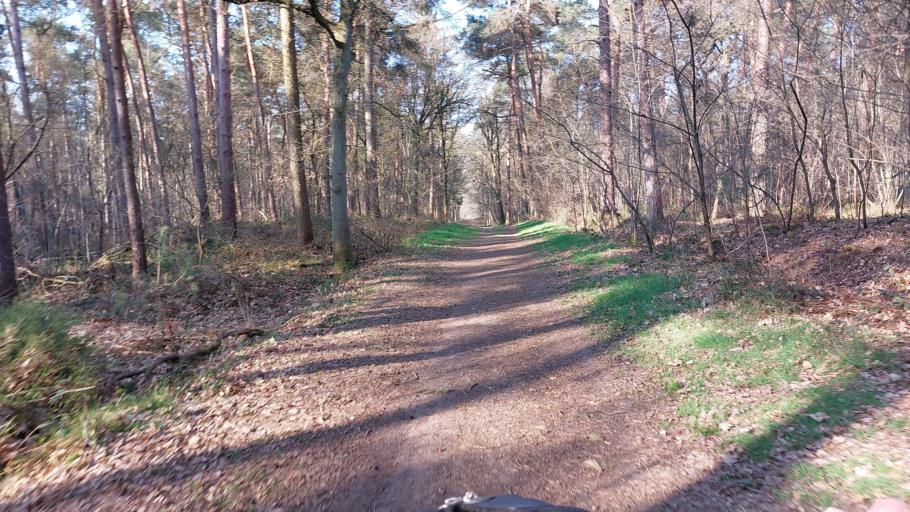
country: BE
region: Wallonia
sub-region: Province du Hainaut
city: Jurbise
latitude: 50.5003
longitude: 3.8638
